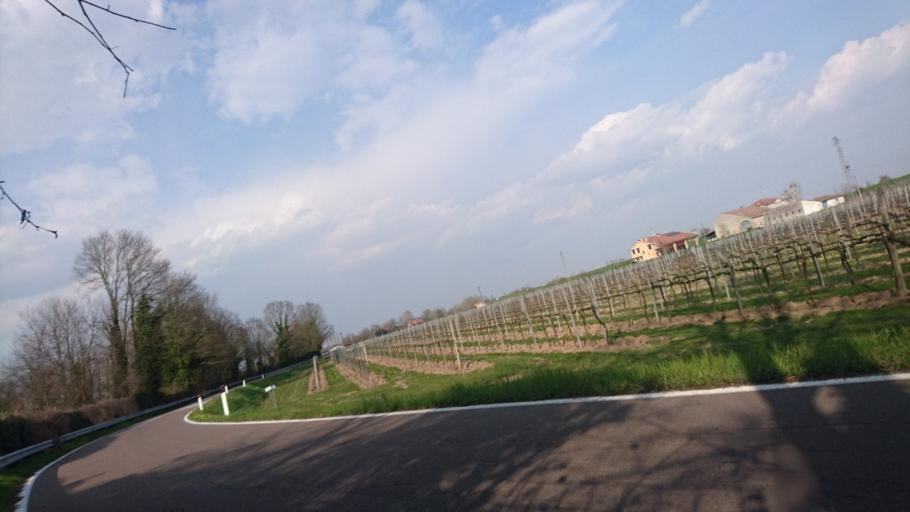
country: IT
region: Veneto
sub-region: Provincia di Padova
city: Battaglia Terme
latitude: 45.3015
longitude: 11.7906
